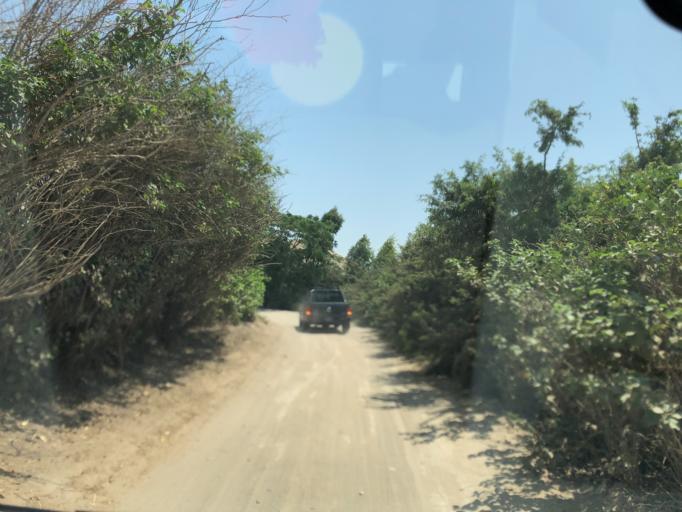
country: PE
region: Lima
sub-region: Provincia de Canete
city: Quilmana
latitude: -13.0051
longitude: -76.4540
